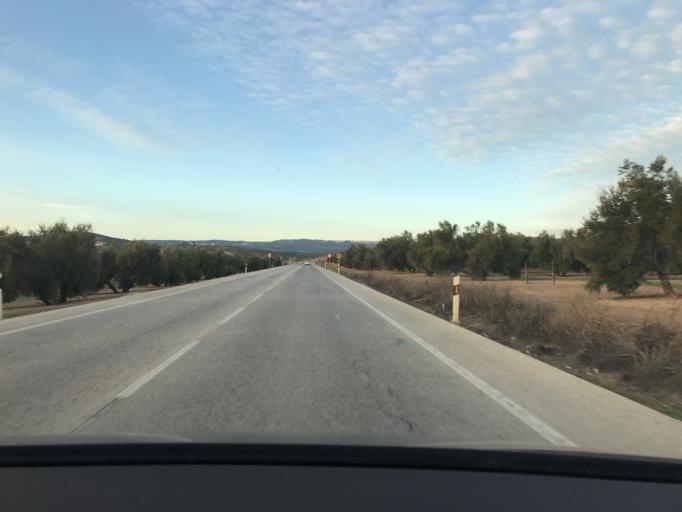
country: ES
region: Andalusia
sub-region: Provincia de Jaen
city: Ubeda
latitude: 37.9370
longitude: -3.3565
